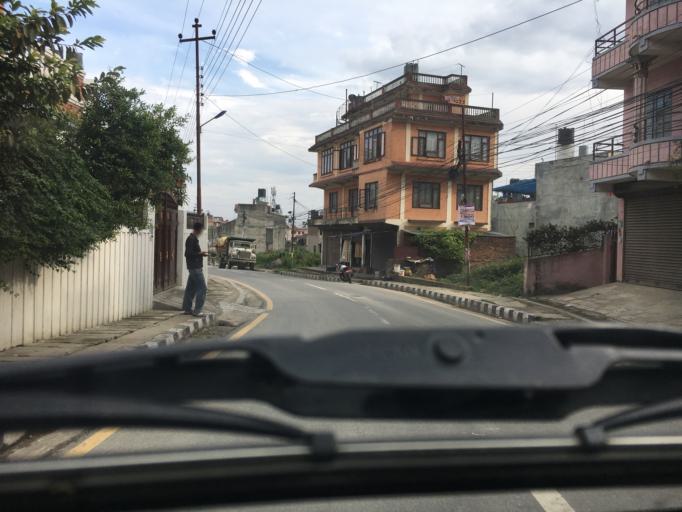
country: NP
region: Central Region
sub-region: Bagmati Zone
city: Kathmandu
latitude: 27.7450
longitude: 85.3473
